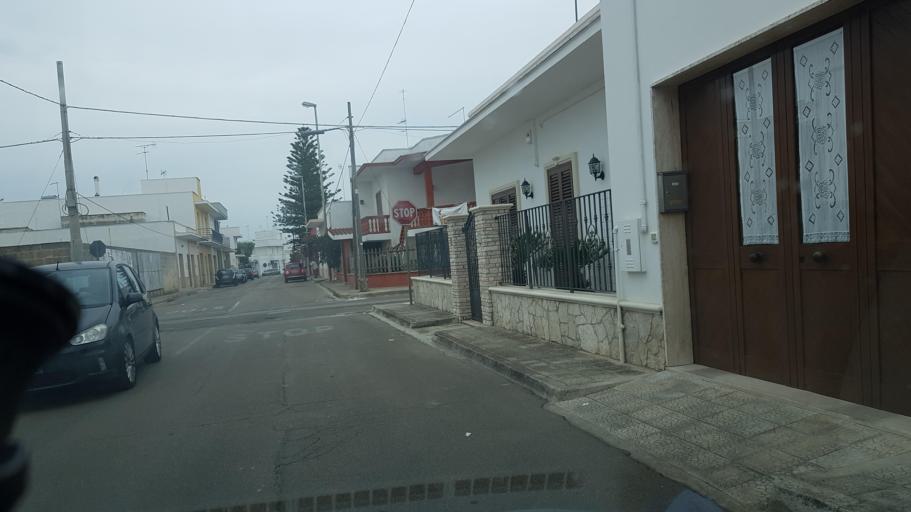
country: IT
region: Apulia
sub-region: Provincia di Lecce
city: Veglie
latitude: 40.3362
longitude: 17.9587
